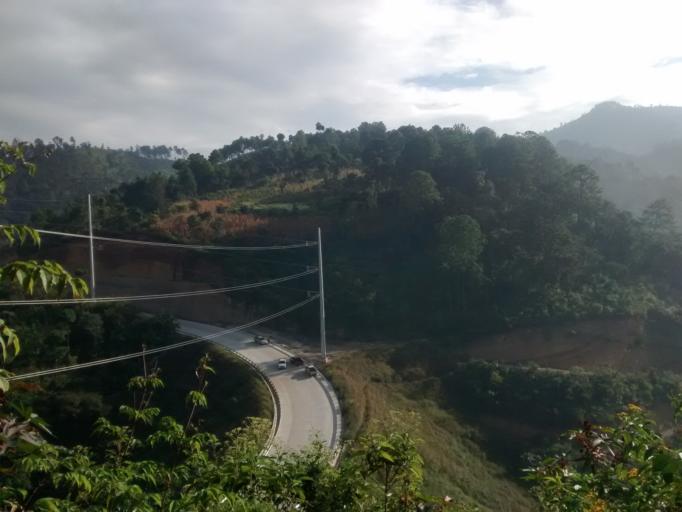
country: GT
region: Sacatepequez
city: Santo Domingo Xenacoj
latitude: 14.6899
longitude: -90.7095
